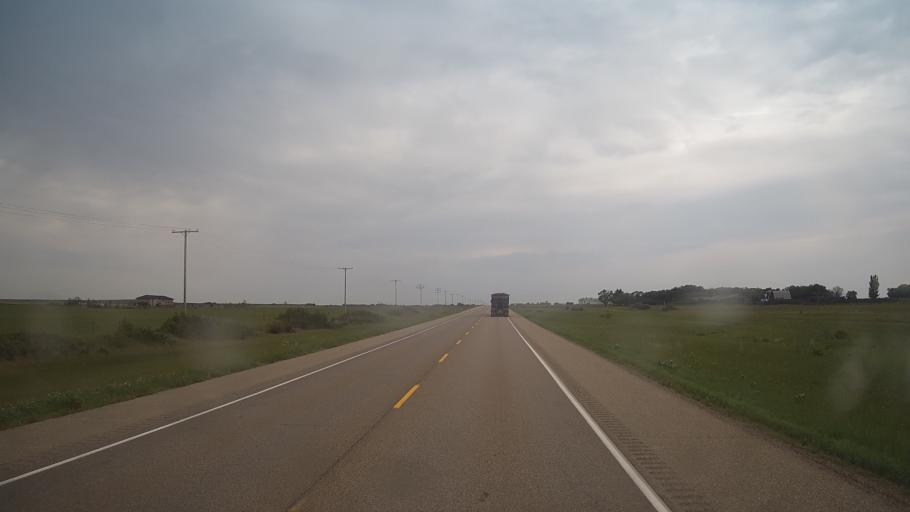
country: CA
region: Saskatchewan
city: Langham
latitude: 52.1288
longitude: -107.1628
